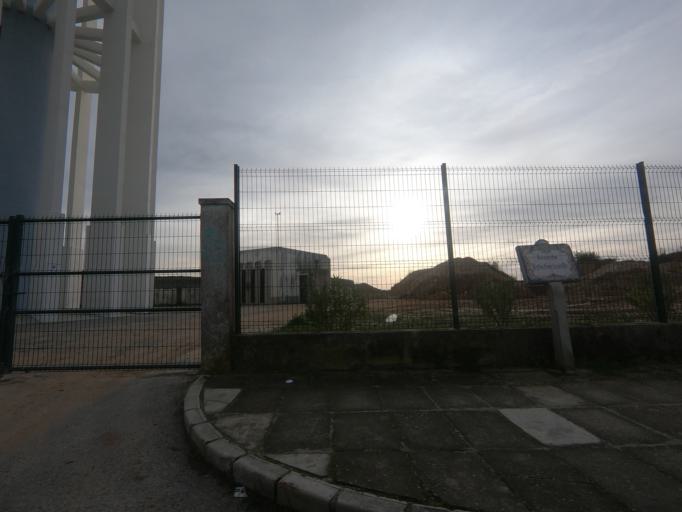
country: PT
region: Setubal
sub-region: Setubal
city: Setubal
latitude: 38.5208
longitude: -8.8721
